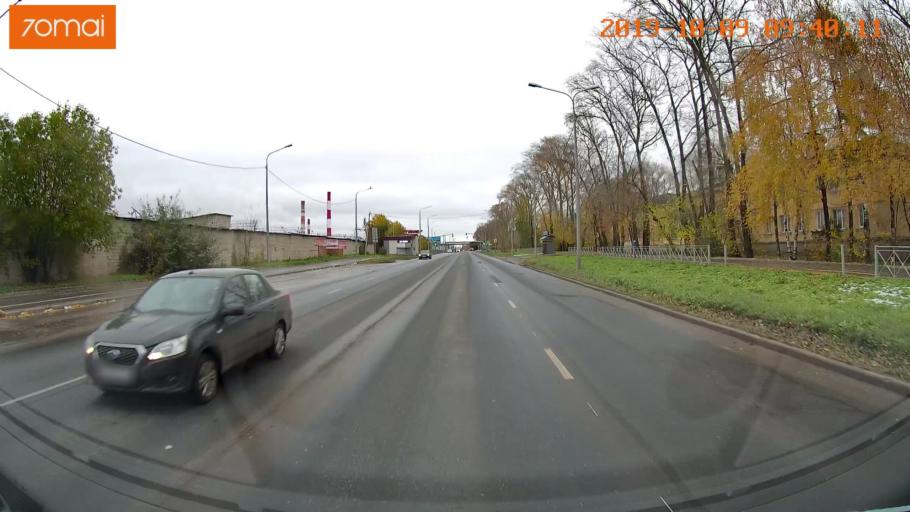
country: RU
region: Vologda
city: Vologda
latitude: 59.1962
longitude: 39.9219
